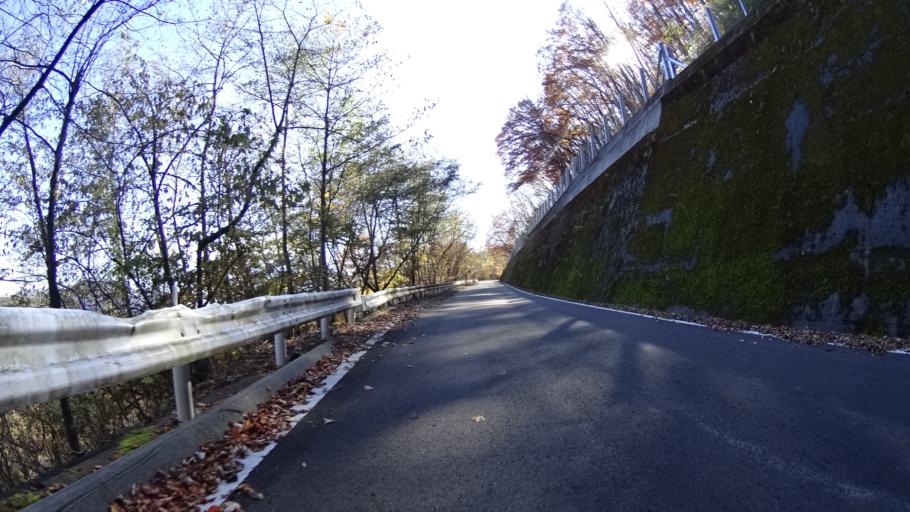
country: JP
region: Yamanashi
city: Otsuki
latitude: 35.7336
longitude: 138.9480
